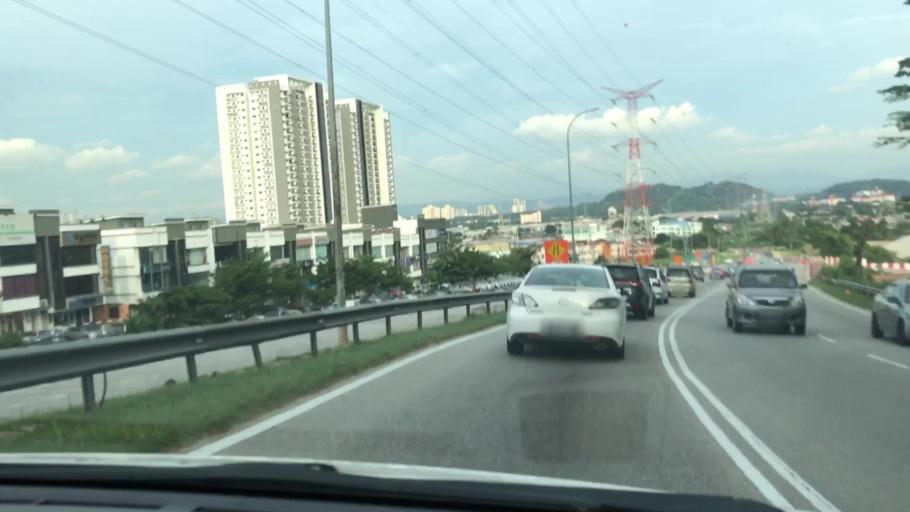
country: MY
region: Selangor
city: Kampong Baharu Balakong
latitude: 3.0125
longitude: 101.6955
